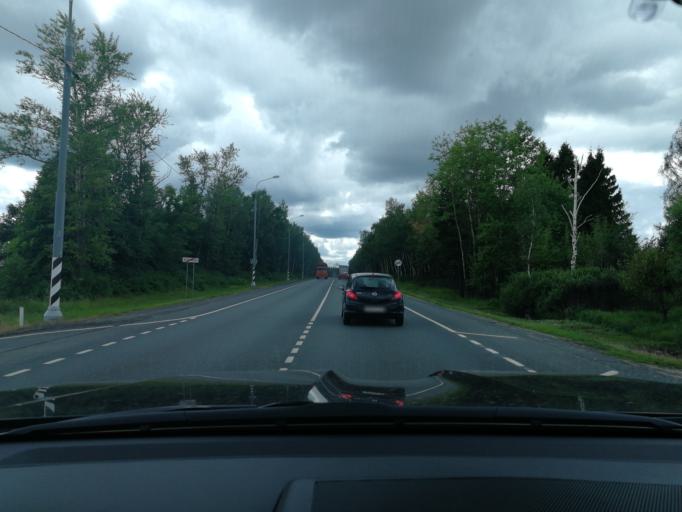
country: RU
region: Moskovskaya
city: Popovo
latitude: 55.0710
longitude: 37.8081
